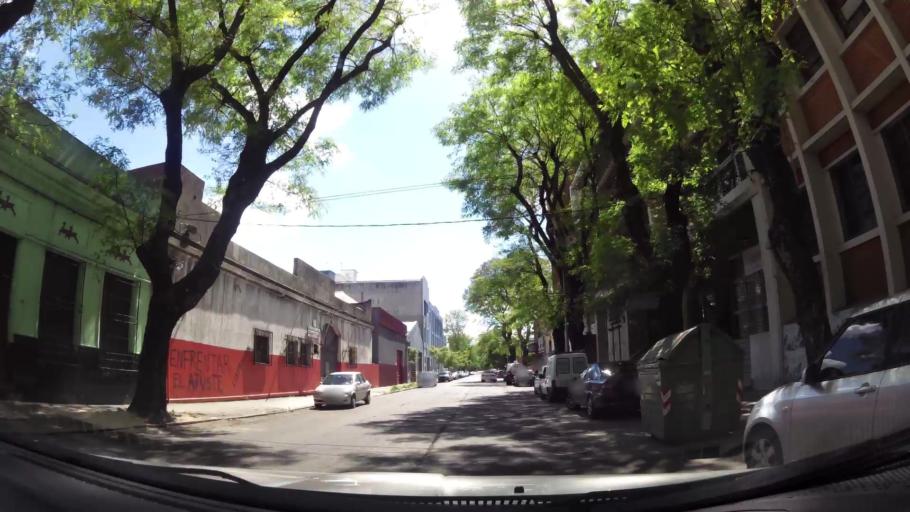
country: UY
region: Montevideo
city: Montevideo
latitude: -34.8846
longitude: -56.1926
